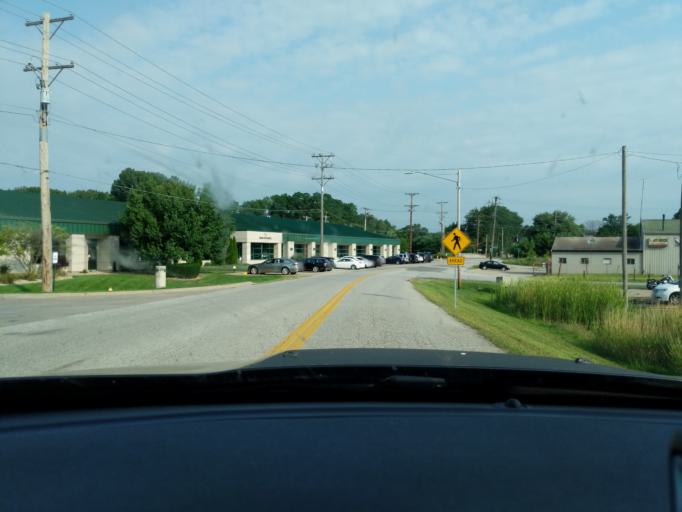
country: US
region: Illinois
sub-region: Rock Island County
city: Rock Island
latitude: 41.5014
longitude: -90.6239
